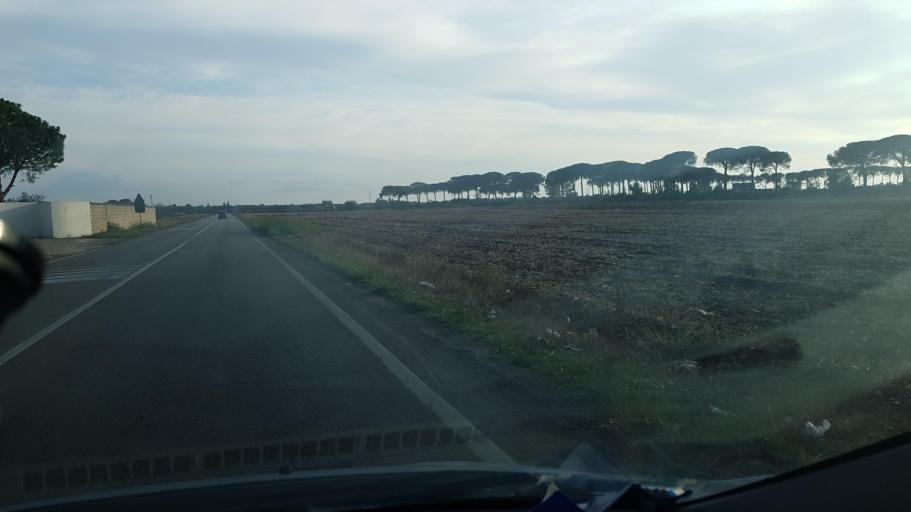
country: IT
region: Apulia
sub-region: Provincia di Lecce
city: Carmiano
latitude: 40.3306
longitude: 18.0394
